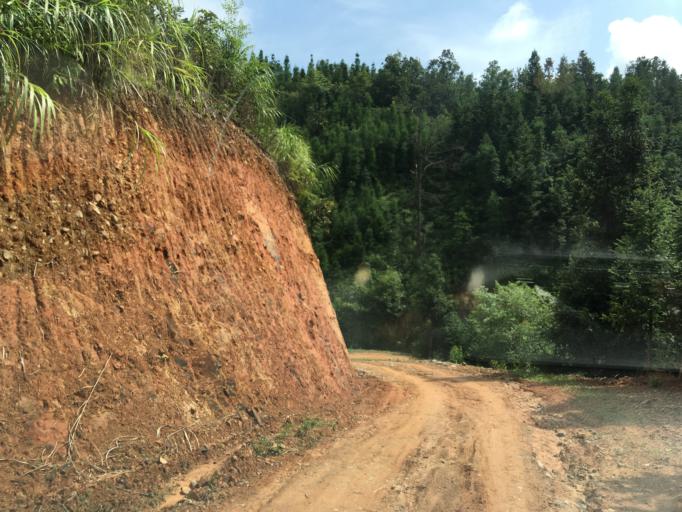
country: CN
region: Guangxi Zhuangzu Zizhiqu
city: Xinzhou
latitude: 24.8660
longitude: 105.8553
